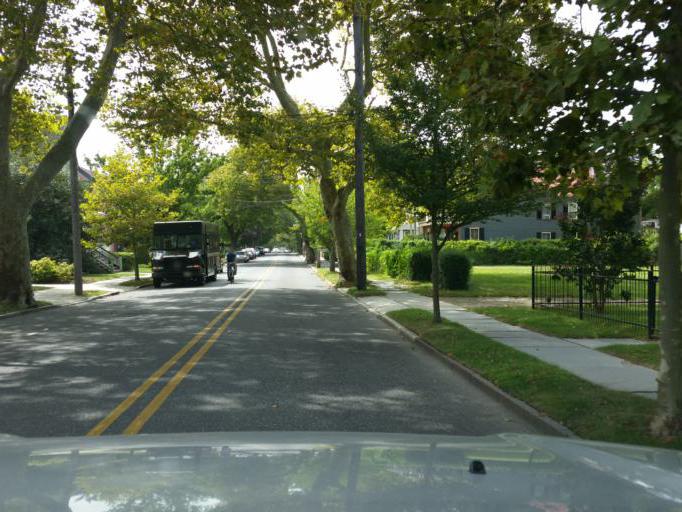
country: US
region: New Jersey
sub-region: Cape May County
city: Cape May
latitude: 38.9374
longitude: -74.9178
